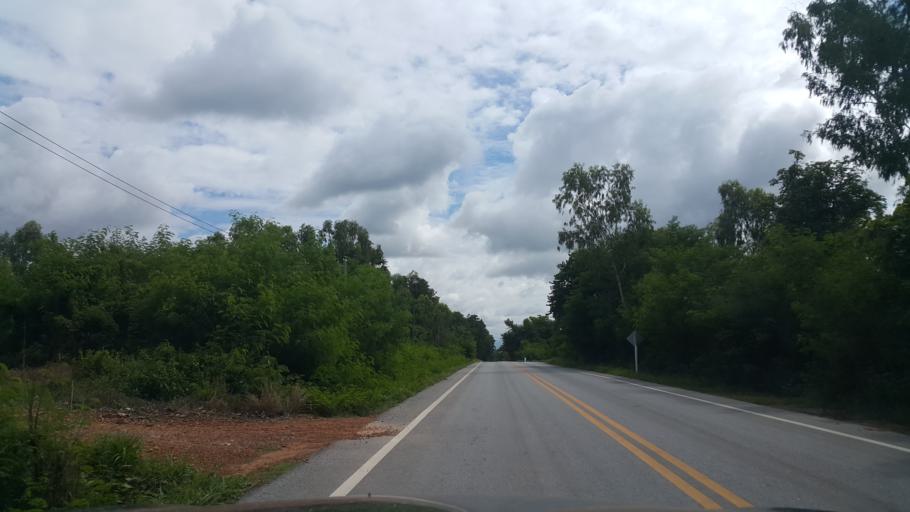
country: TH
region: Uttaradit
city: Thong Saen Khan
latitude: 17.3865
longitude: 100.2897
